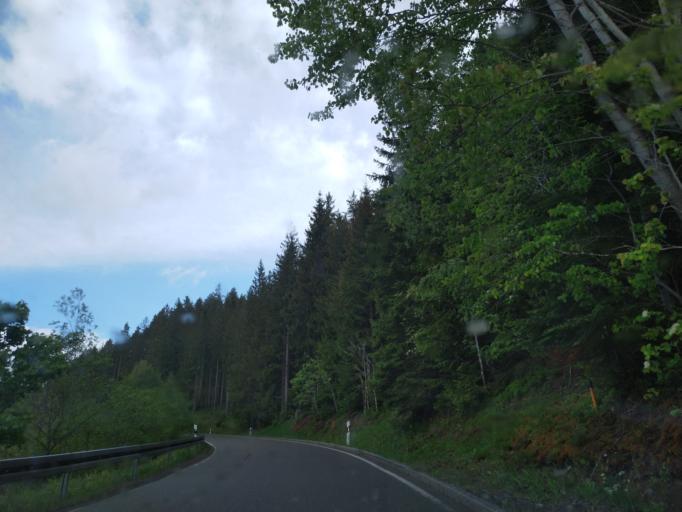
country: DE
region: Baden-Wuerttemberg
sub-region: Freiburg Region
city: Friedenweiler
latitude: 47.9221
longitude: 8.2574
